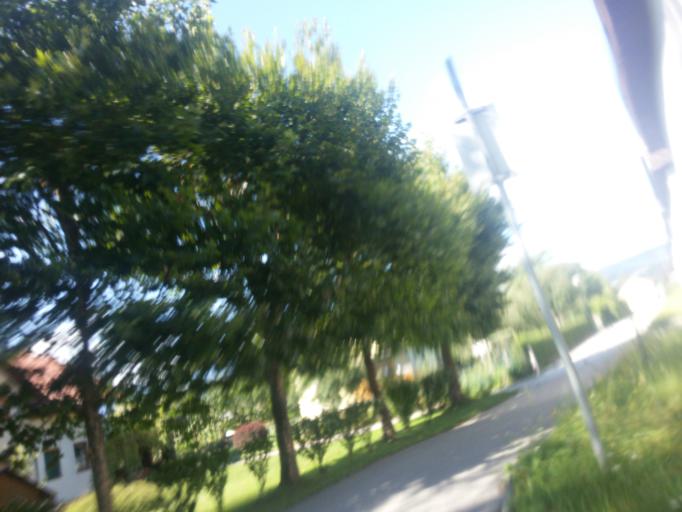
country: AT
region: Carinthia
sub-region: Politischer Bezirk Villach Land
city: Wernberg
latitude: 46.6069
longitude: 13.9140
